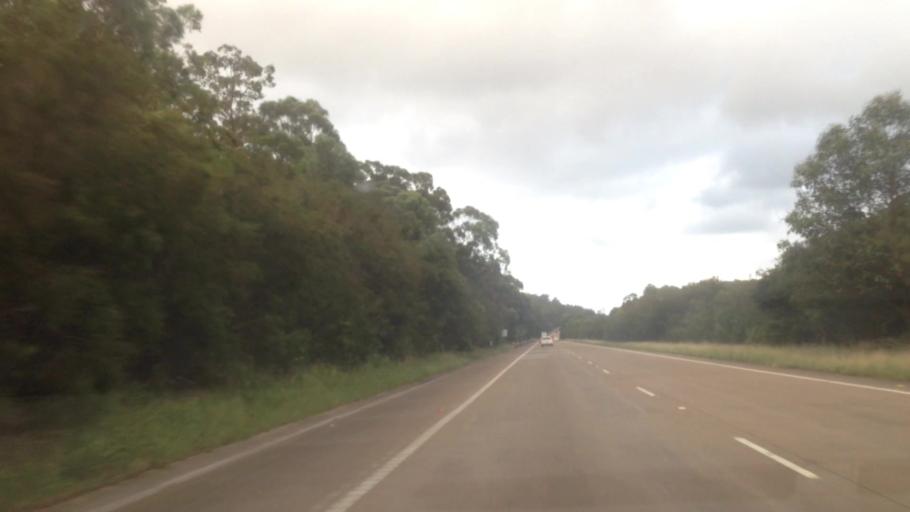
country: AU
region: New South Wales
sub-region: Wyong Shire
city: Charmhaven
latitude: -33.1617
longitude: 151.4691
